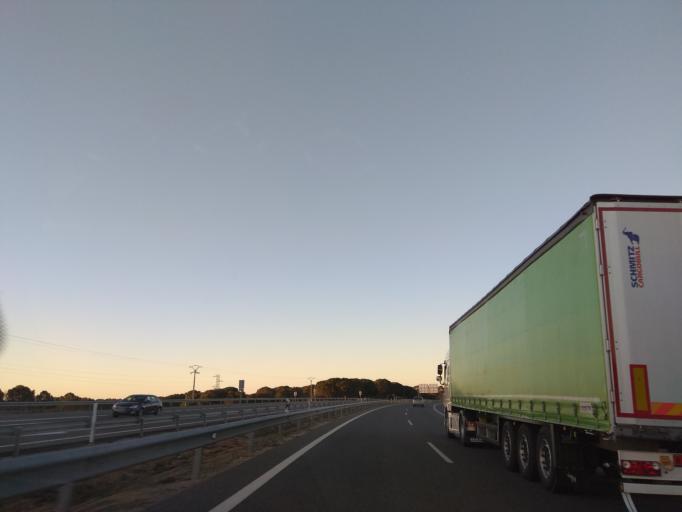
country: ES
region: Castille and Leon
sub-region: Provincia de Burgos
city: Aranda de Duero
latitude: 41.7169
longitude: -3.6887
